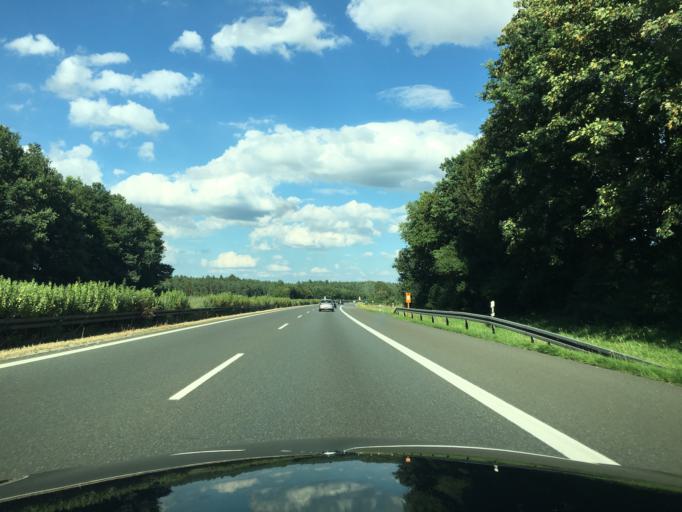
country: DE
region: Bavaria
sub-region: Regierungsbezirk Mittelfranken
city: Petersaurach
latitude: 49.3045
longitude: 10.7652
